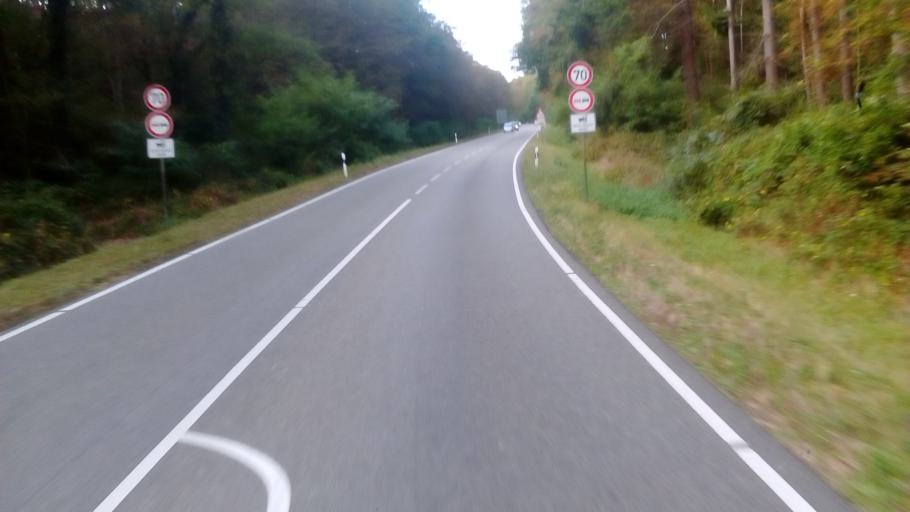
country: DE
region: Rheinland-Pfalz
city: Berg
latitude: 49.0085
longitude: 8.1851
